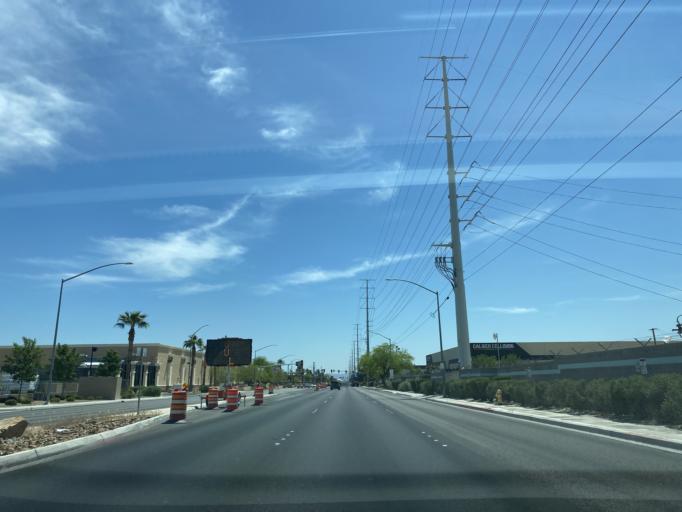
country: US
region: Nevada
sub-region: Clark County
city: North Las Vegas
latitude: 36.2441
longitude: -115.1169
